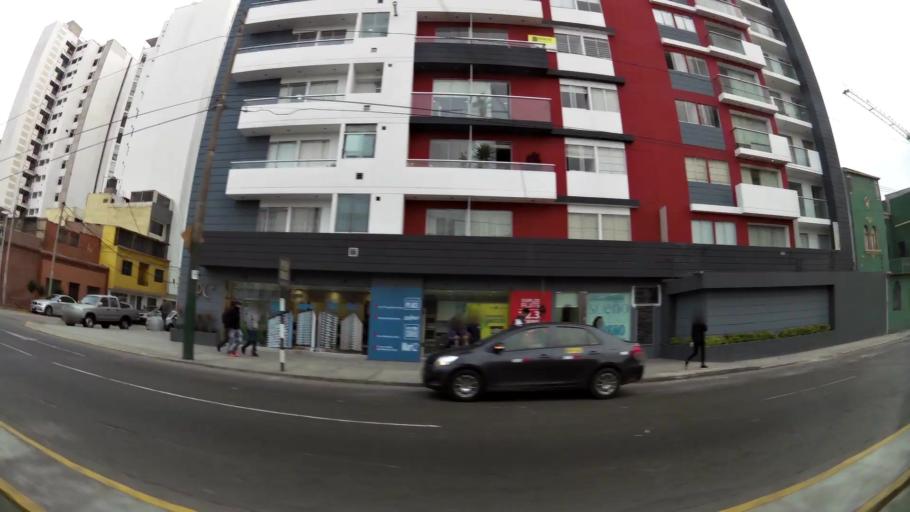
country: PE
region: Lima
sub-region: Lima
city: San Isidro
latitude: -12.0975
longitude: -77.0707
